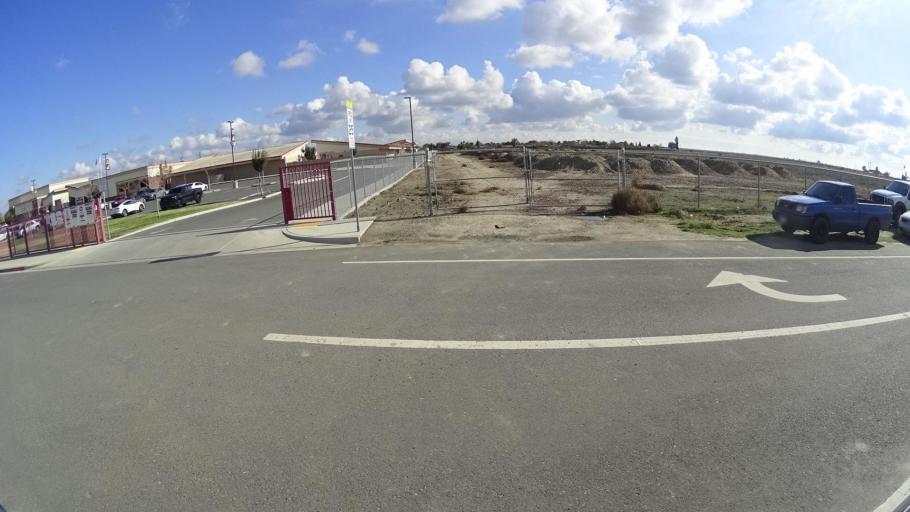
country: US
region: California
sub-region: Kern County
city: McFarland
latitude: 35.6656
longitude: -119.2415
